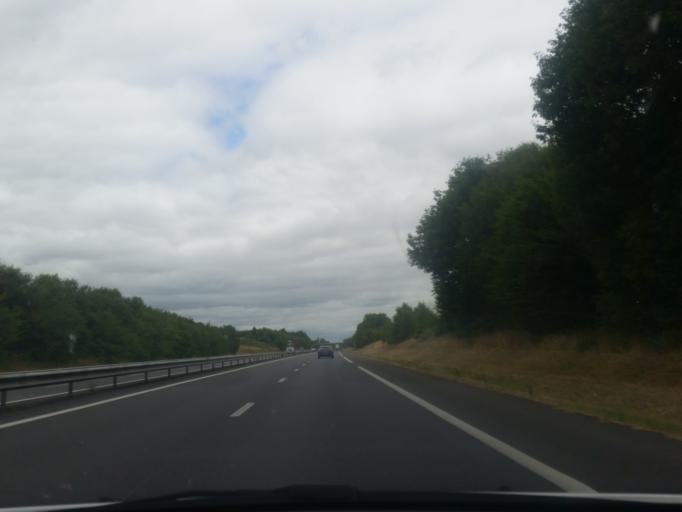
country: FR
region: Pays de la Loire
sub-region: Departement de Maine-et-Loire
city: Durtal
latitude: 47.7256
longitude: -0.2504
